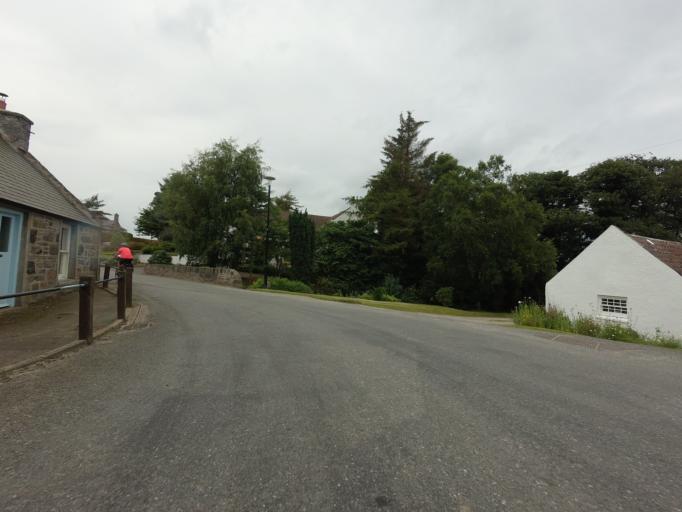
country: GB
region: Scotland
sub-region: Aberdeenshire
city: Portsoy
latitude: 57.6624
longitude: -2.7470
